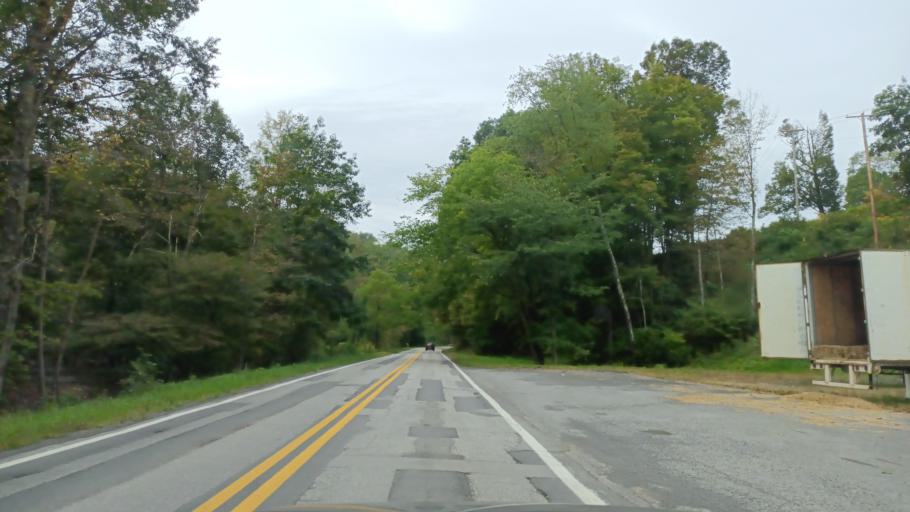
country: US
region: West Virginia
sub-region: Taylor County
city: Grafton
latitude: 39.3289
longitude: -79.8395
